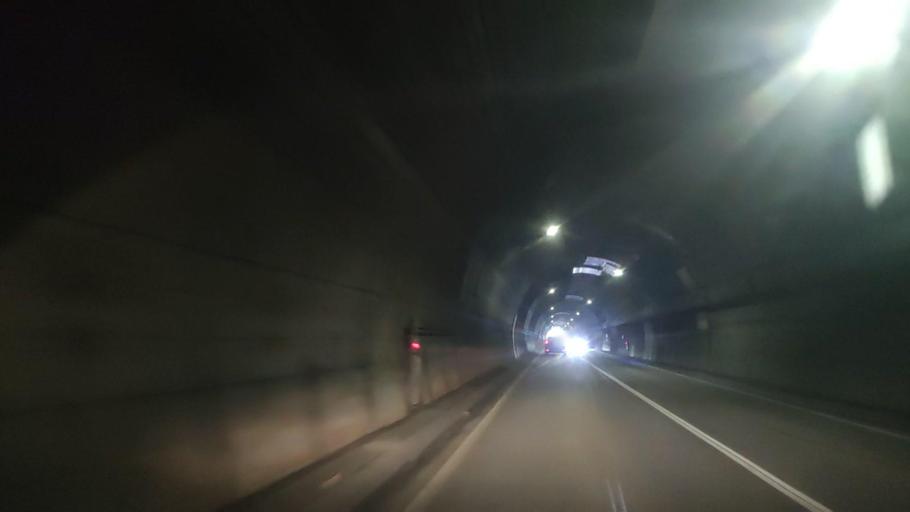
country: JP
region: Hokkaido
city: Nanae
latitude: 42.1209
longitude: 140.5309
